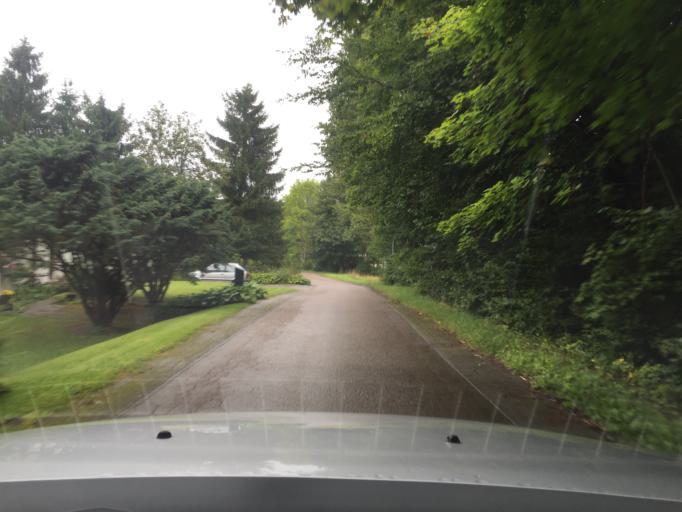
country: SE
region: Skane
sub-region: Hassleholms Kommun
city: Sosdala
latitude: 56.0055
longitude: 13.6396
